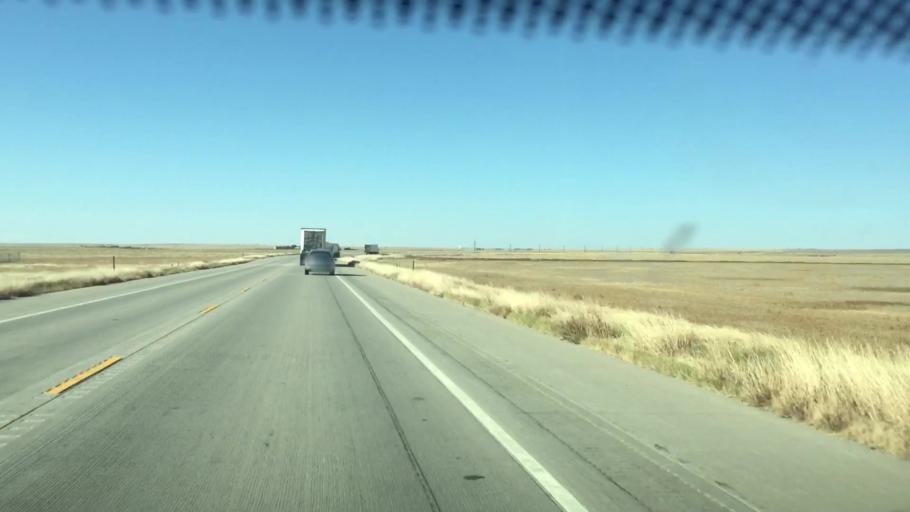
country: US
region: Colorado
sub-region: Kiowa County
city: Eads
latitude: 38.3717
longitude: -102.7279
